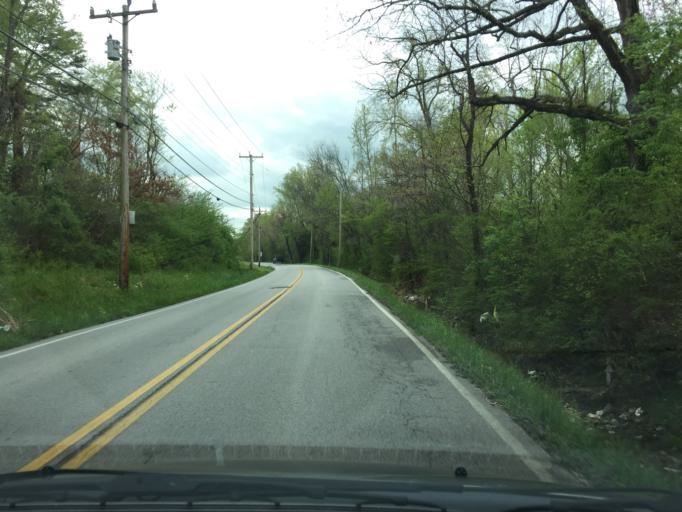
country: US
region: Tennessee
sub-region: Hamilton County
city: Falling Water
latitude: 35.1542
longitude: -85.2444
